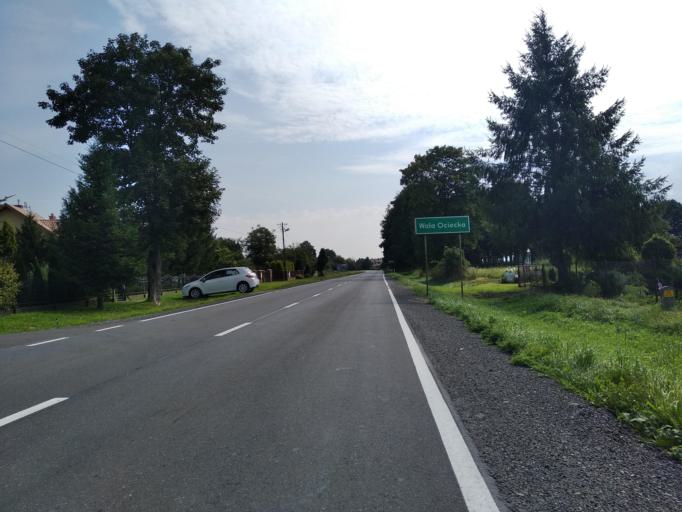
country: PL
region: Subcarpathian Voivodeship
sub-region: Powiat mielecki
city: Przeclaw
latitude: 50.1650
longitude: 21.5112
